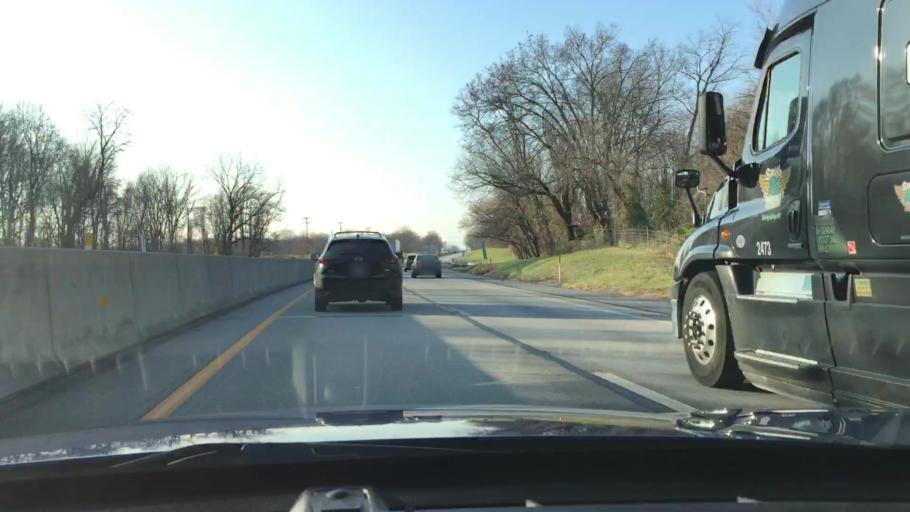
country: US
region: Pennsylvania
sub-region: Cumberland County
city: Mechanicsburg
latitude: 40.1967
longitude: -77.0231
